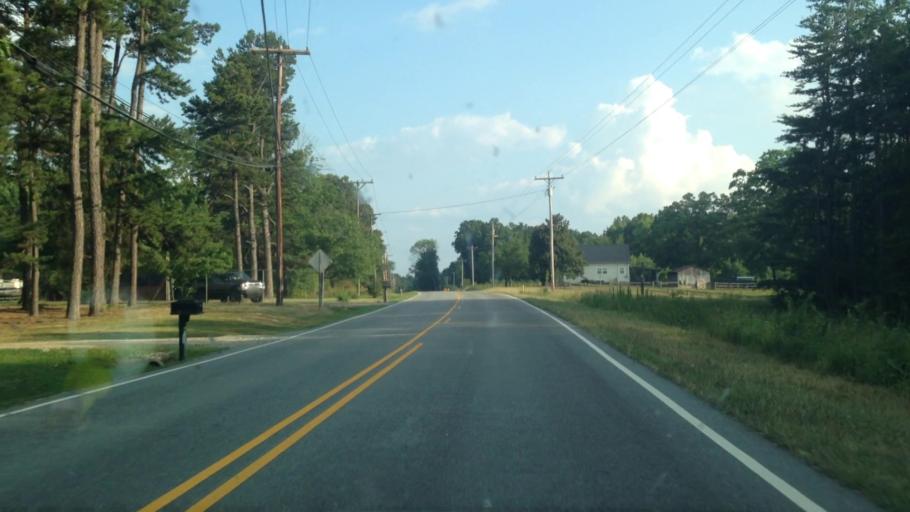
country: US
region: North Carolina
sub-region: Guilford County
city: High Point
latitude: 35.9995
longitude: -80.0631
